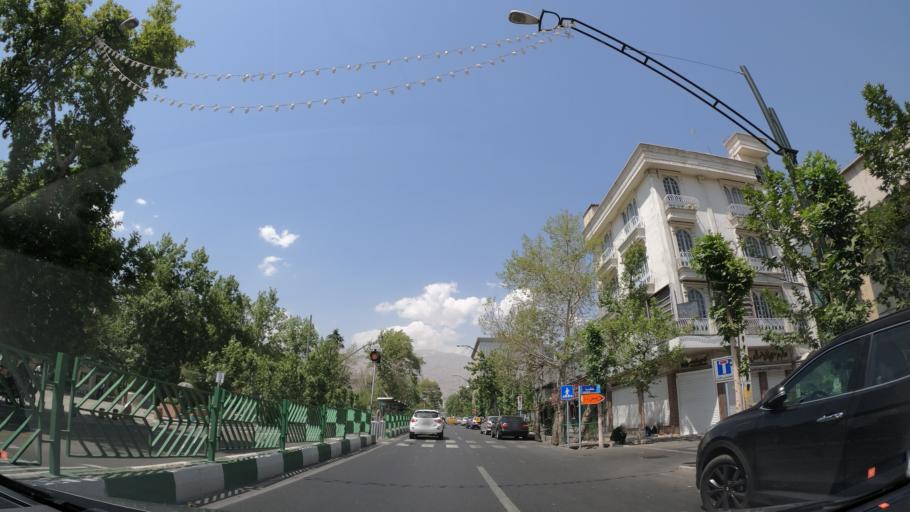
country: IR
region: Tehran
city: Tajrish
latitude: 35.7773
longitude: 51.4133
